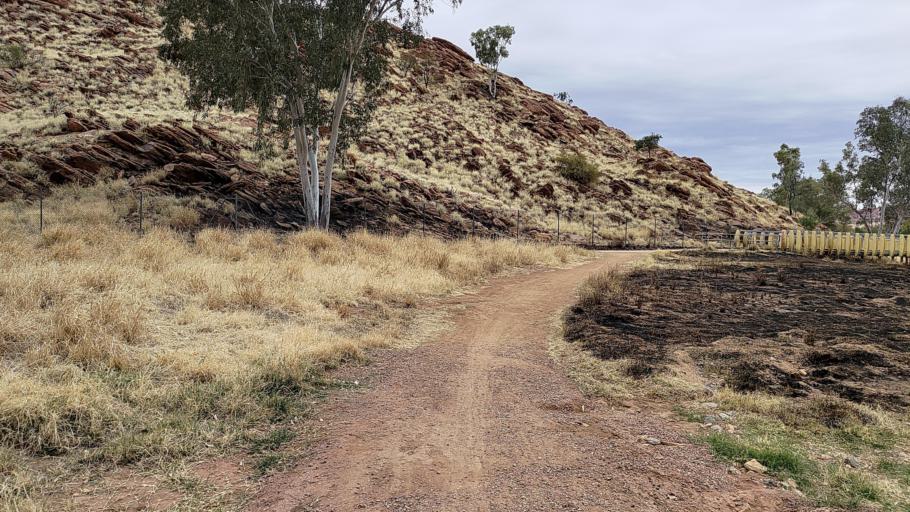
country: AU
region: Northern Territory
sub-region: Alice Springs
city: Alice Springs
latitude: -23.7034
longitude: 133.8845
